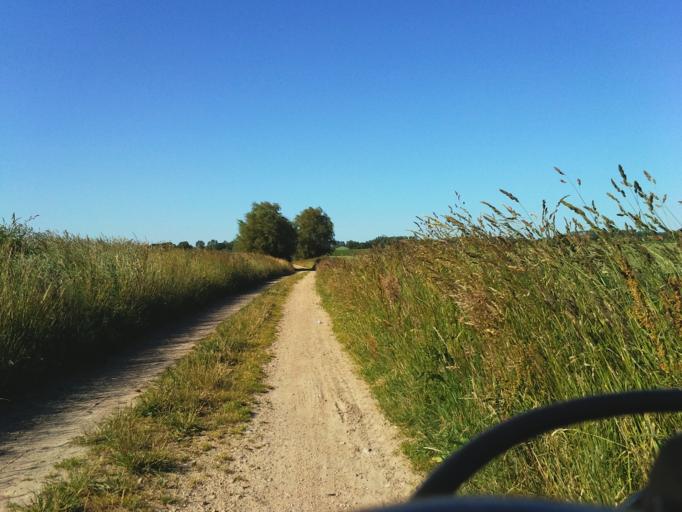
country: DE
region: Mecklenburg-Vorpommern
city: Nienhagen
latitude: 54.1494
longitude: 12.1909
